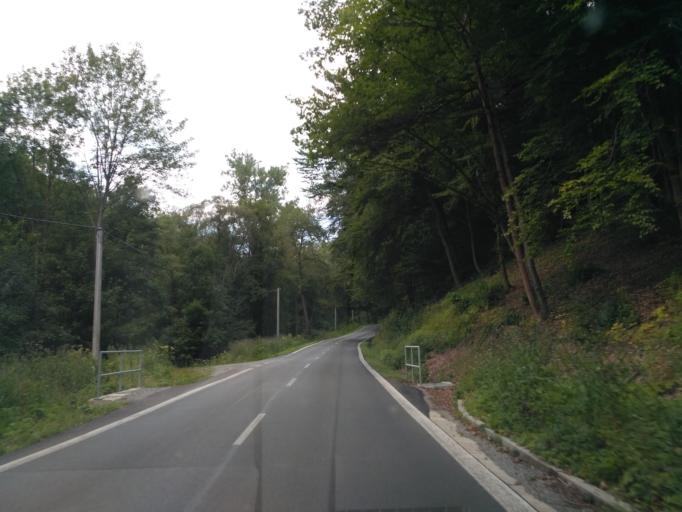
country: SK
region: Kosicky
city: Gelnica
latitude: 48.9043
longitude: 21.0250
